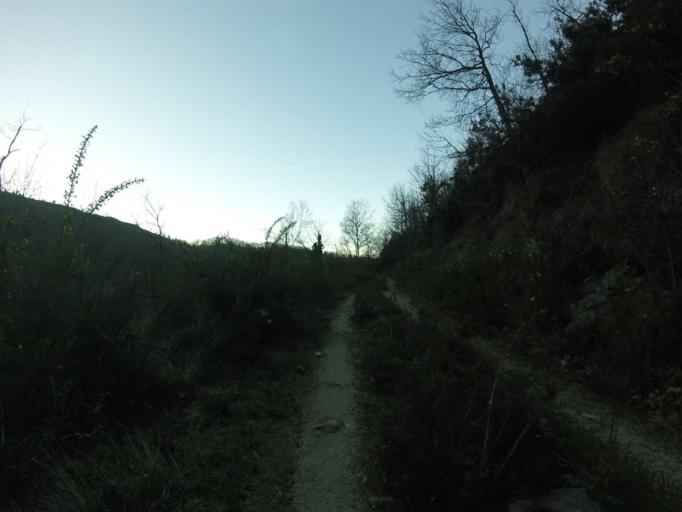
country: ES
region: Navarre
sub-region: Provincia de Navarra
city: Arano
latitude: 43.2533
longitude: -1.8395
